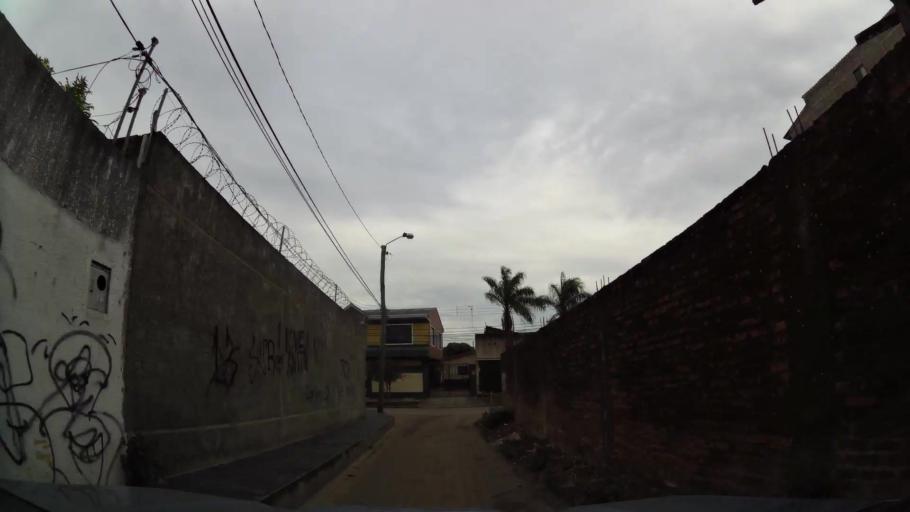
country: BO
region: Santa Cruz
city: Santa Cruz de la Sierra
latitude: -17.7706
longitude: -63.1647
